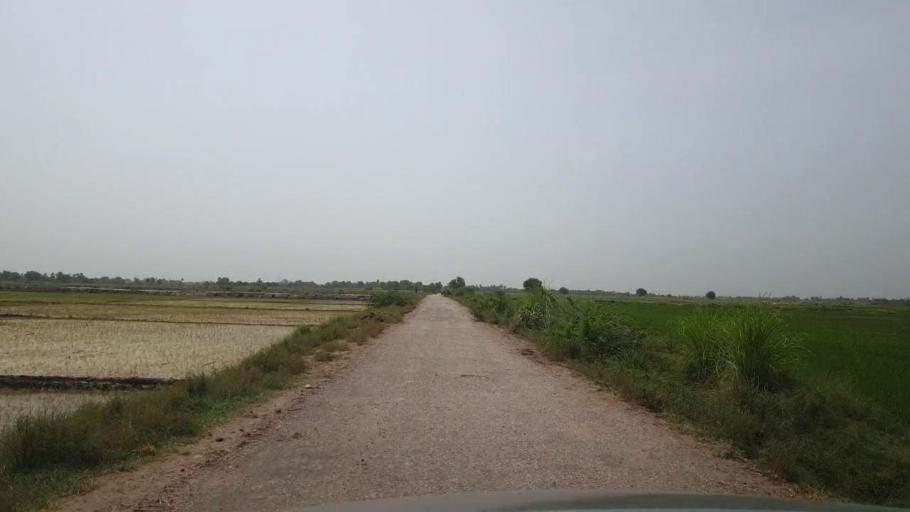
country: PK
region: Sindh
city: Madeji
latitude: 27.8348
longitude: 68.4261
